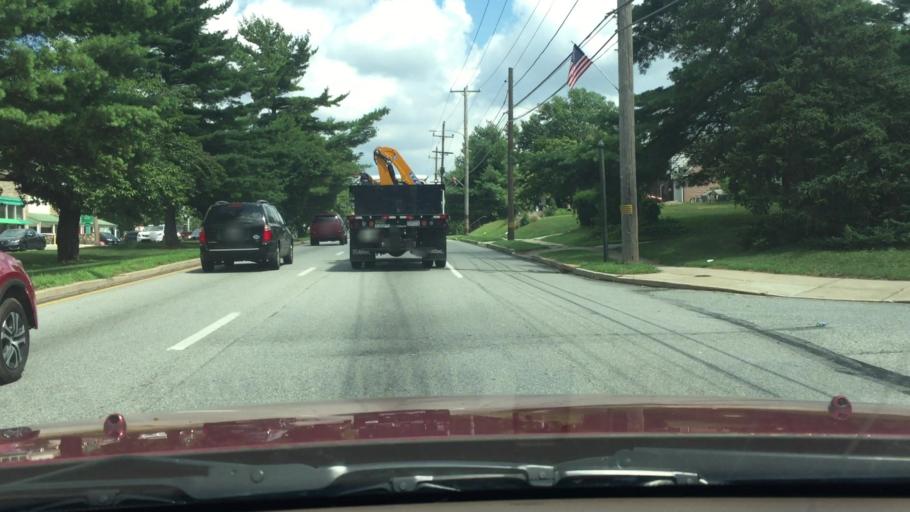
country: US
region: Pennsylvania
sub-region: Delaware County
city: Broomall
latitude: 39.9739
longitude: -75.3250
